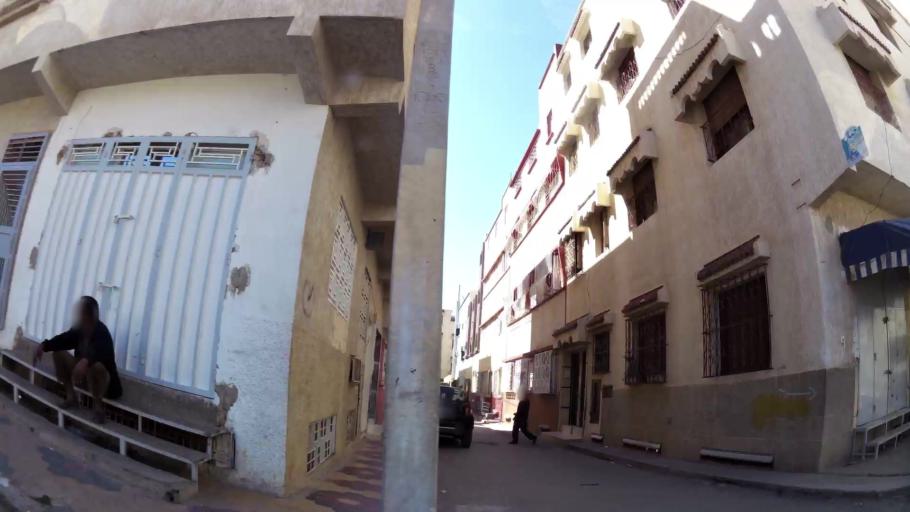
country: MA
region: Meknes-Tafilalet
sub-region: Meknes
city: Meknes
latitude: 33.8845
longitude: -5.5737
